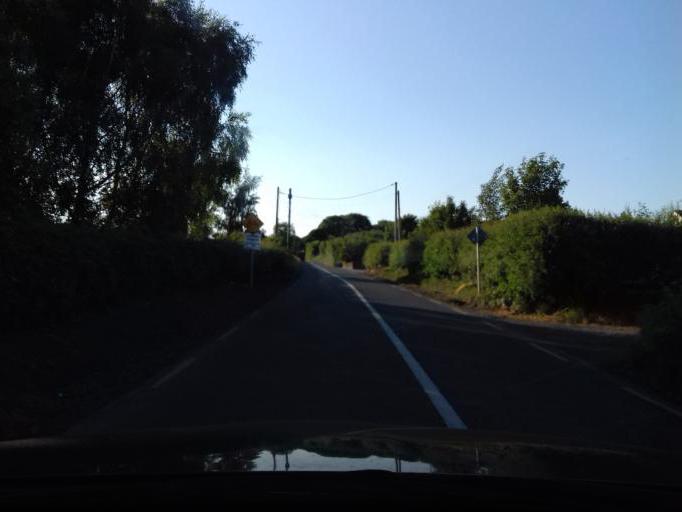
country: IE
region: Leinster
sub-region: An Mhi
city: Ashbourne
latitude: 53.5588
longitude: -6.3827
